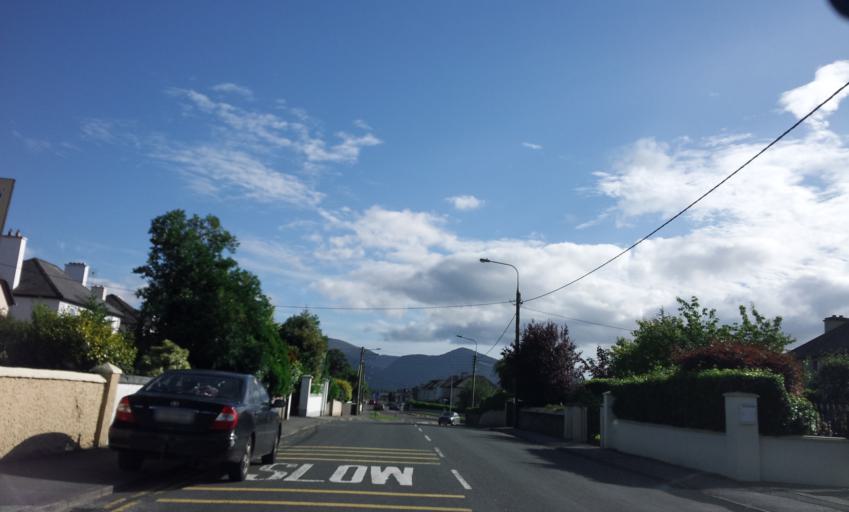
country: IE
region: Munster
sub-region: Ciarrai
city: Cill Airne
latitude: 52.0651
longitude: -9.5060
